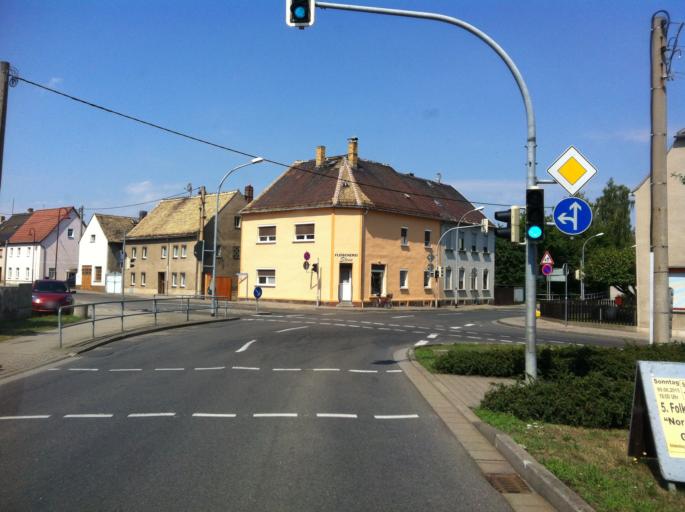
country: DE
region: Saxony
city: Trebsen
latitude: 51.2888
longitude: 12.7551
